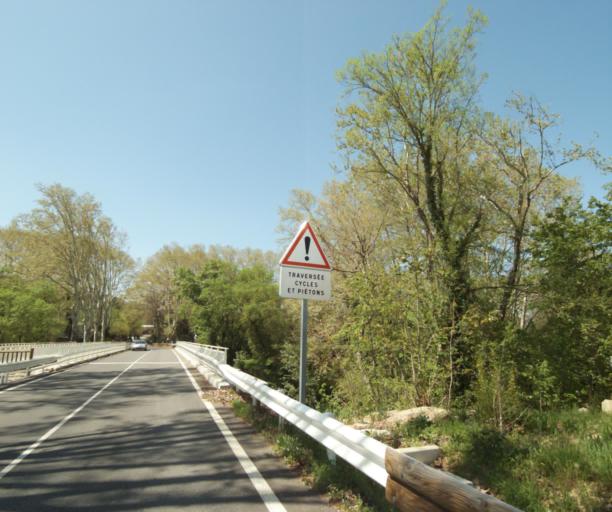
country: FR
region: Languedoc-Roussillon
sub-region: Departement de l'Herault
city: Prades-le-Lez
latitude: 43.7015
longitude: 3.8577
